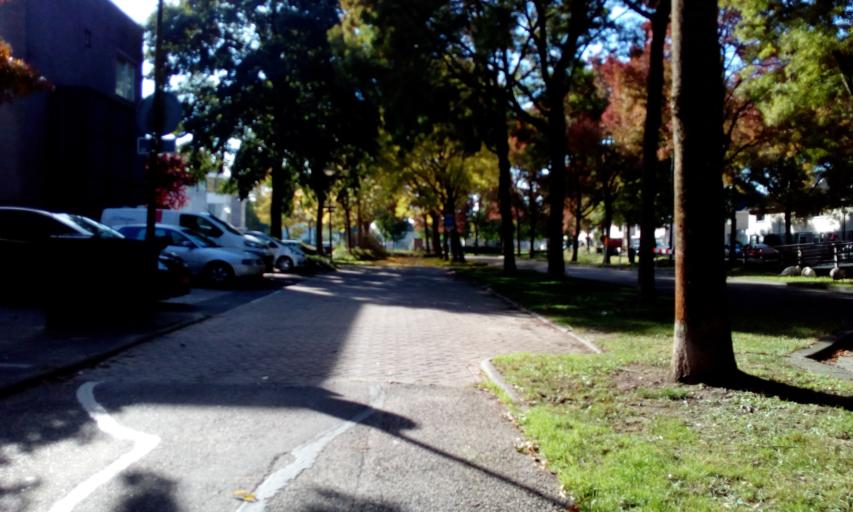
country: NL
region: Utrecht
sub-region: Stichtse Vecht
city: Spechtenkamp
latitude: 52.0874
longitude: 5.0279
